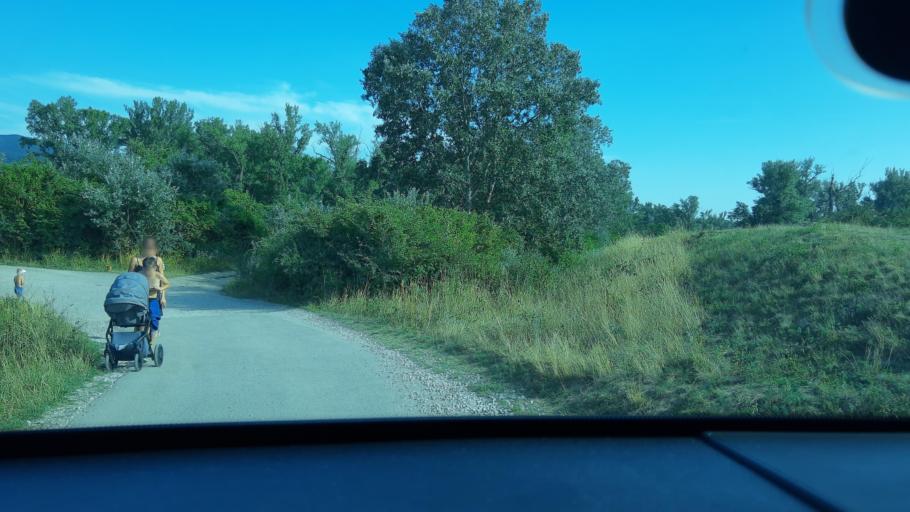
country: SK
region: Trnavsky
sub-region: Okres Trnava
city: Piestany
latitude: 48.6099
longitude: 17.8455
